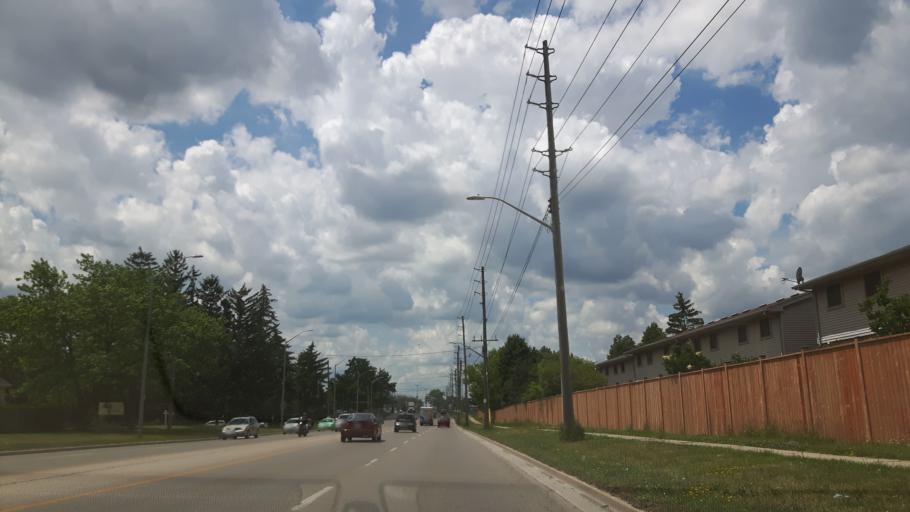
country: CA
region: Ontario
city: London
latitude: 42.9416
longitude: -81.2484
